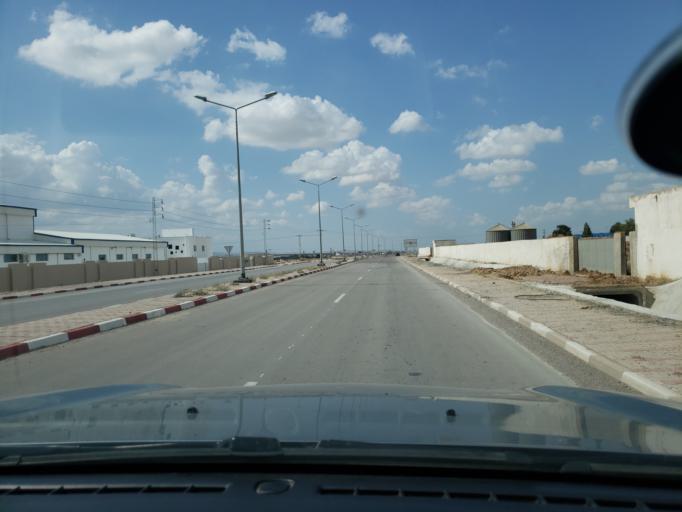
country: TN
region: Tunis
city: La Mohammedia
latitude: 36.5617
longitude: 10.0845
